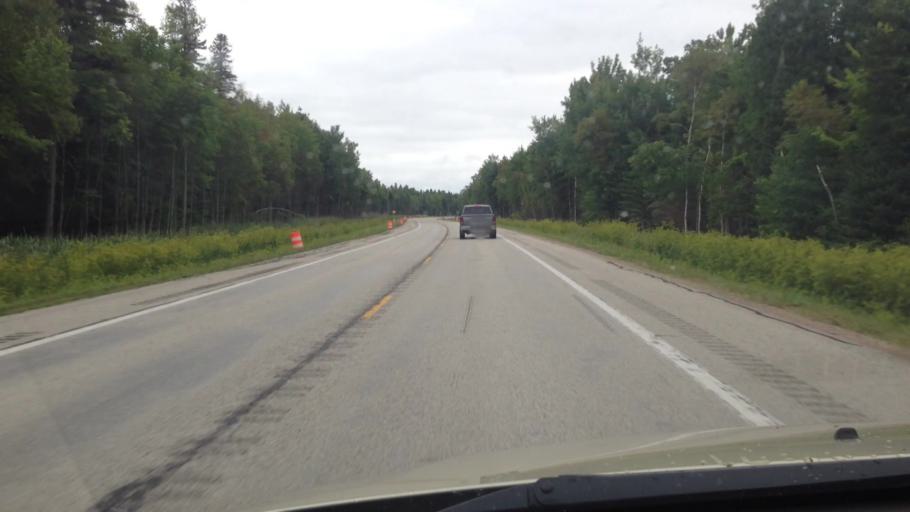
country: US
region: Michigan
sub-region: Delta County
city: Escanaba
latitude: 45.5867
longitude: -87.2389
